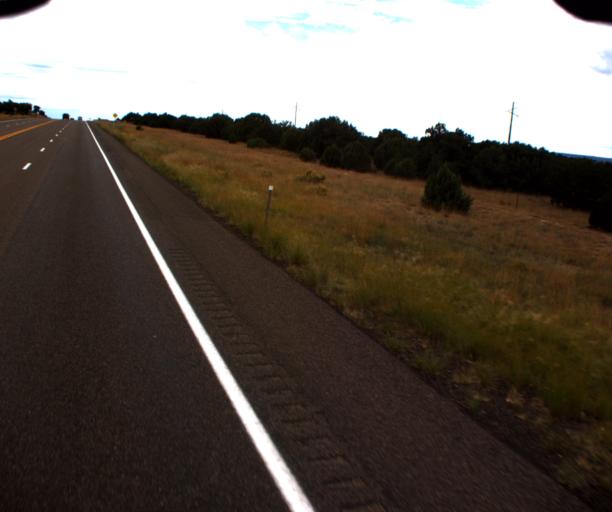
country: US
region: Arizona
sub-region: Navajo County
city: White Mountain Lake
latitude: 34.3369
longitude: -110.0494
